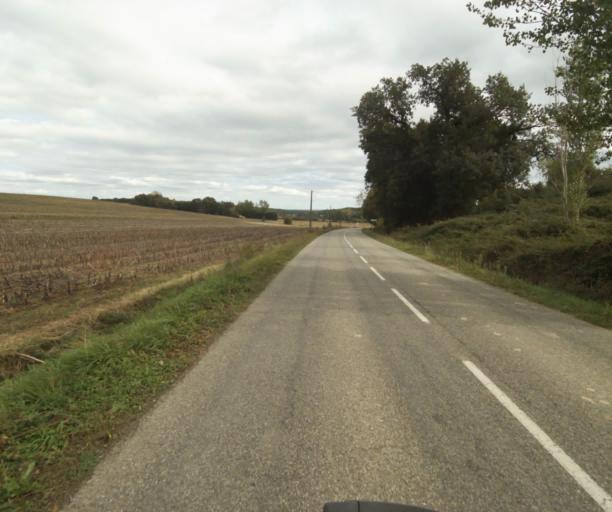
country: FR
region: Midi-Pyrenees
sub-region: Departement du Tarn-et-Garonne
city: Verdun-sur-Garonne
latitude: 43.8573
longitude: 1.1231
